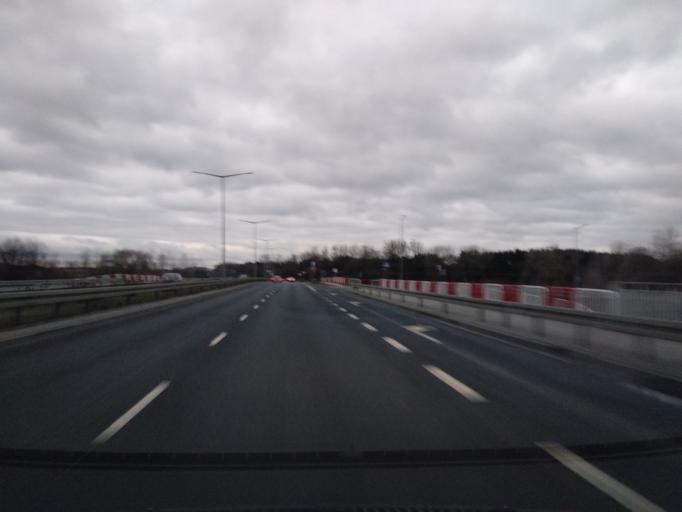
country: PL
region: Greater Poland Voivodeship
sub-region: Konin
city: Konin
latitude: 52.2125
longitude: 18.2279
